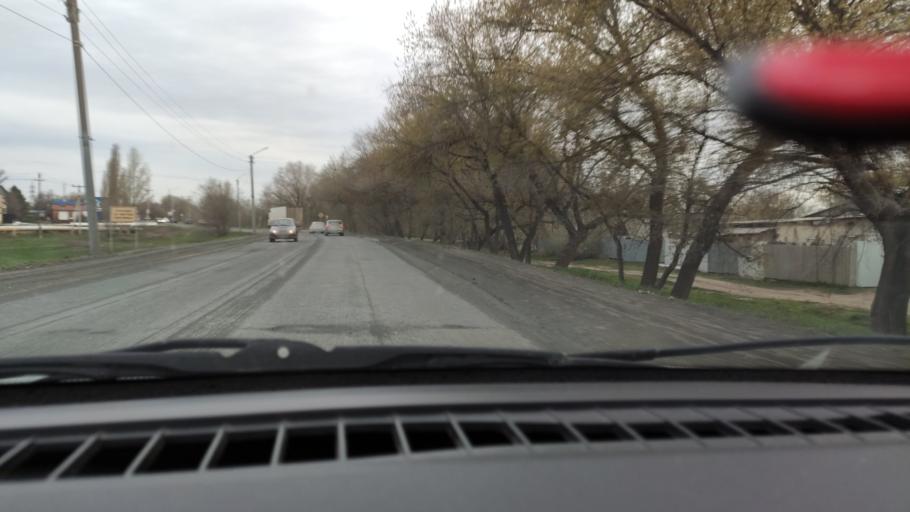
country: RU
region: Orenburg
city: Orenburg
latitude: 51.8599
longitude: 55.1342
